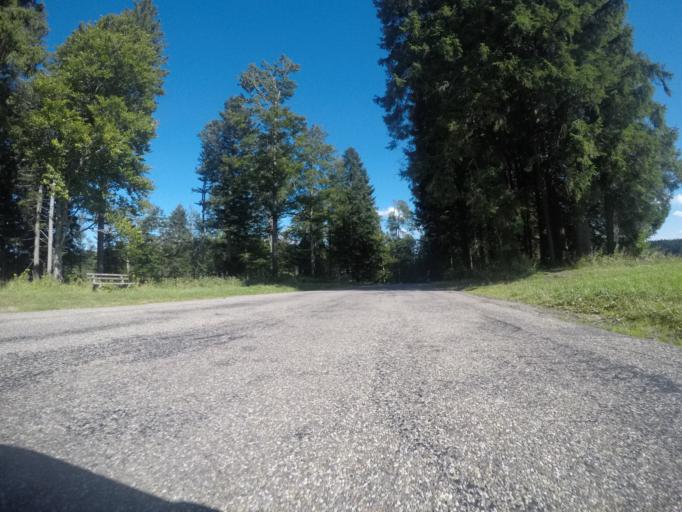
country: DE
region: Baden-Wuerttemberg
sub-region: Freiburg Region
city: Gutenbach
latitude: 48.0638
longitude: 8.1735
